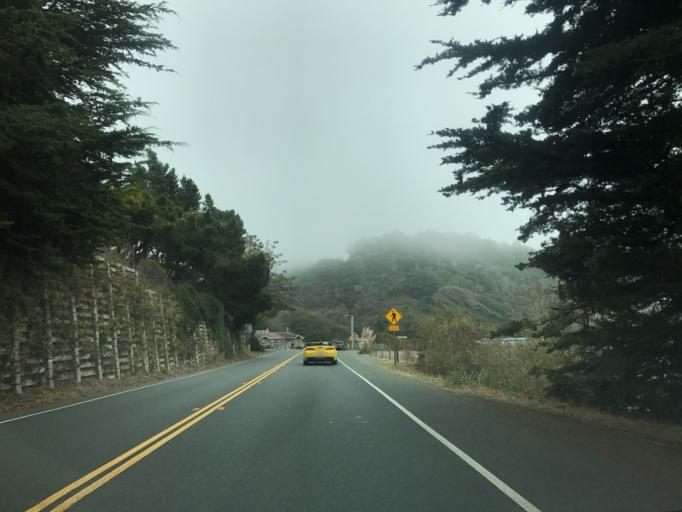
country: US
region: California
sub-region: Sonoma County
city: Monte Rio
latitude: 38.4501
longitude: -123.1167
